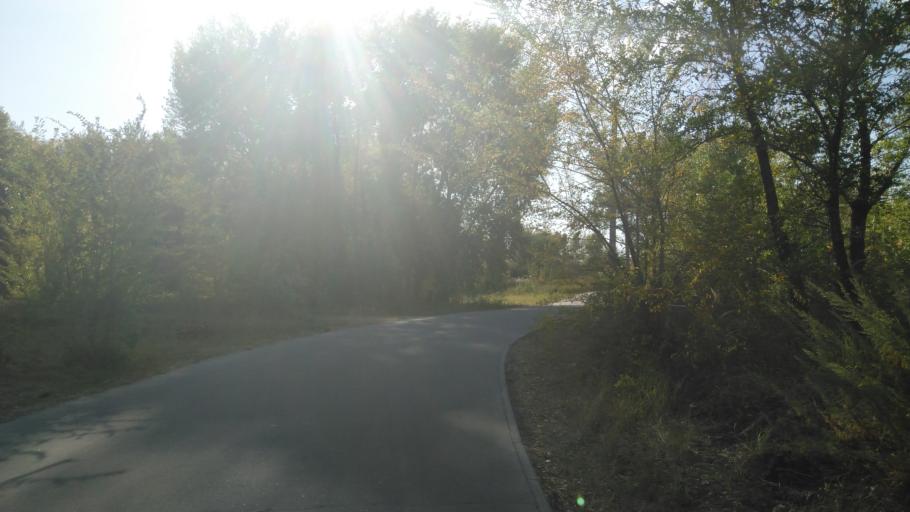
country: KZ
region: Pavlodar
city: Pavlodar
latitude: 52.2605
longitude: 76.9352
